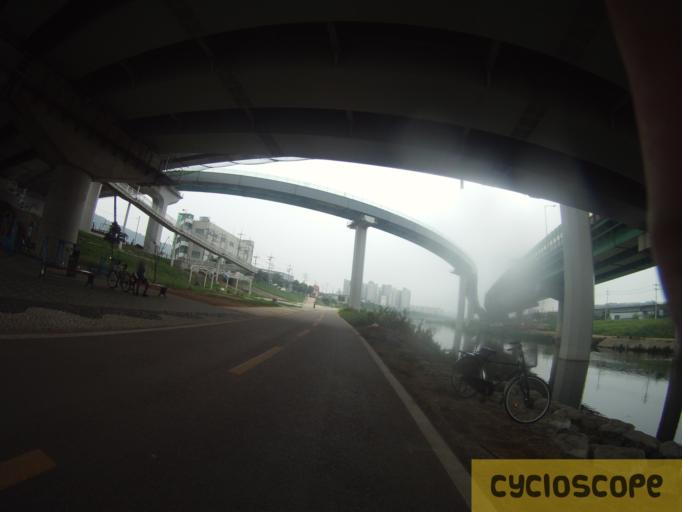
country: KR
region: Gyeonggi-do
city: Kwangmyong
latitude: 37.4412
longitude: 126.8998
